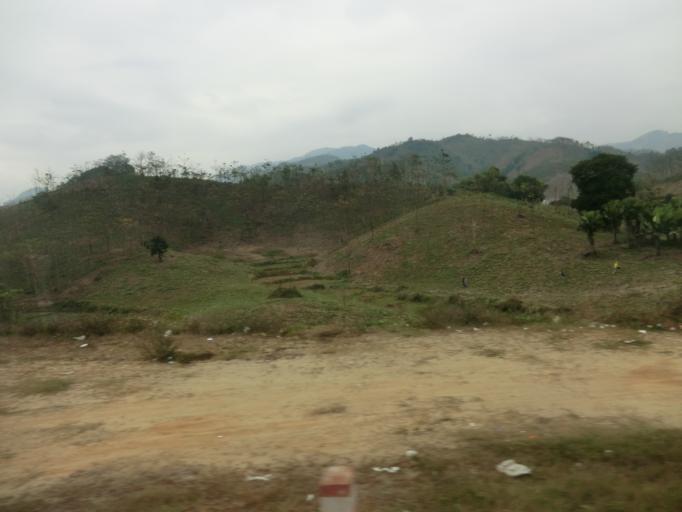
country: VN
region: Lao Cai
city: Thi Tran Pho Rang
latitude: 22.0798
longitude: 104.4579
